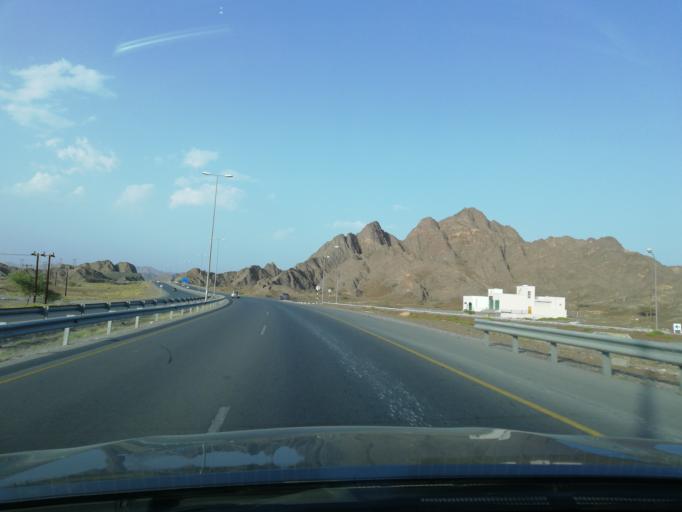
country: OM
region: Muhafazat ad Dakhiliyah
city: Izki
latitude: 22.9159
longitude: 57.7765
